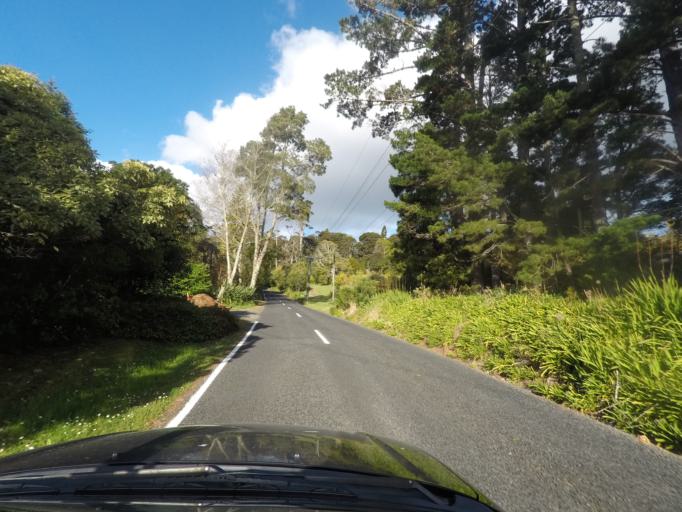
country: NZ
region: Auckland
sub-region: Auckland
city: Titirangi
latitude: -36.9404
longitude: 174.6205
